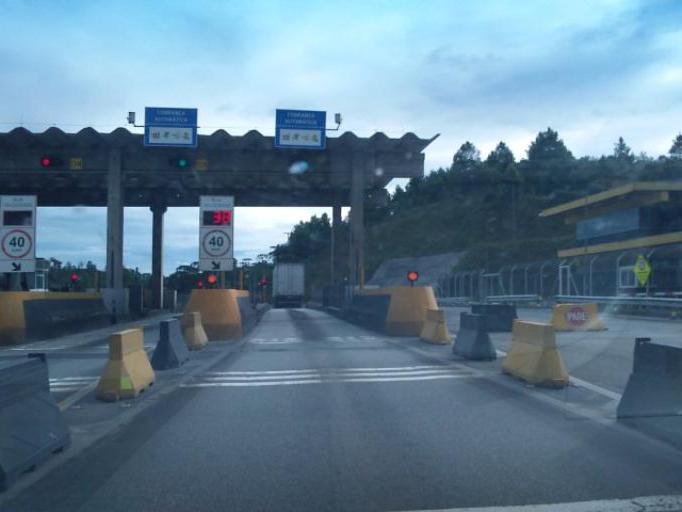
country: BR
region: Parana
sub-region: Campina Grande Do Sul
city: Campina Grande do Sul
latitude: -25.2888
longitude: -48.9341
